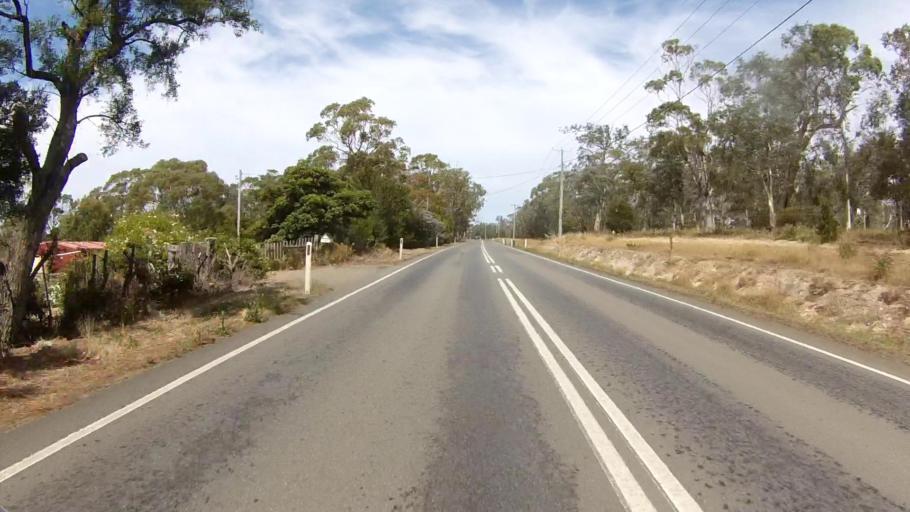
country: AU
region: Tasmania
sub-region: Clarence
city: Sandford
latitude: -42.9691
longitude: 147.5033
